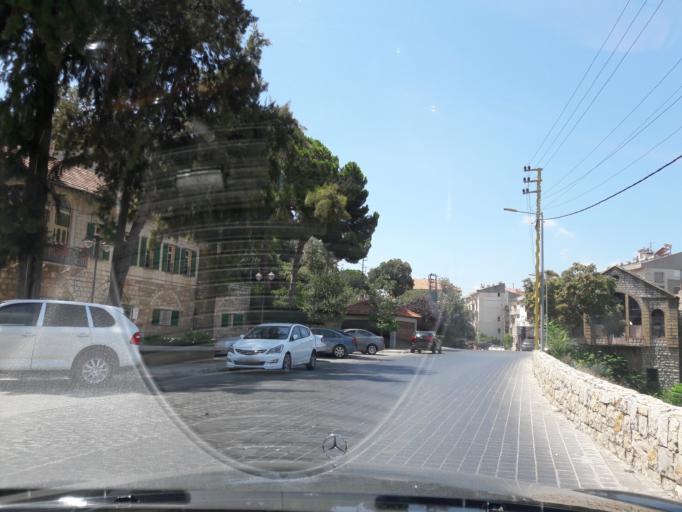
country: LB
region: Mont-Liban
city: Djounie
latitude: 33.9213
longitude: 35.6421
